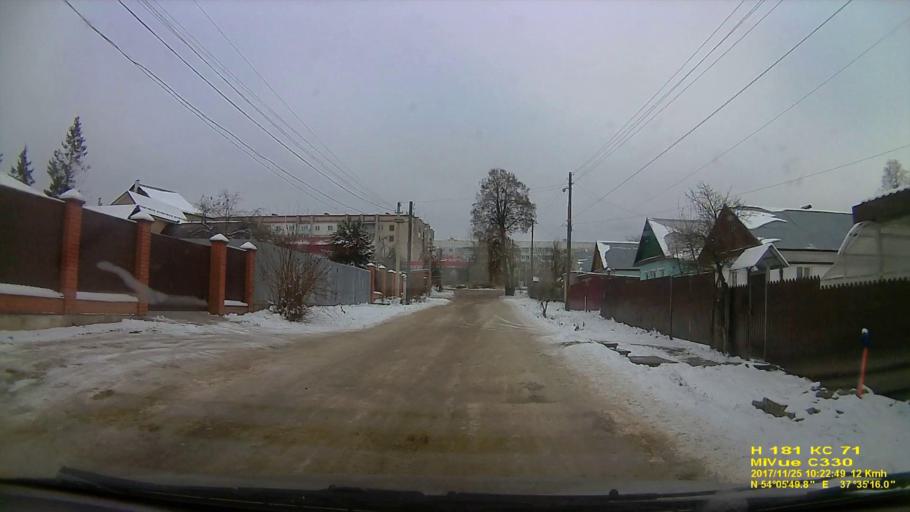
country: RU
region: Tula
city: Skuratovskiy
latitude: 54.0971
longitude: 37.5878
